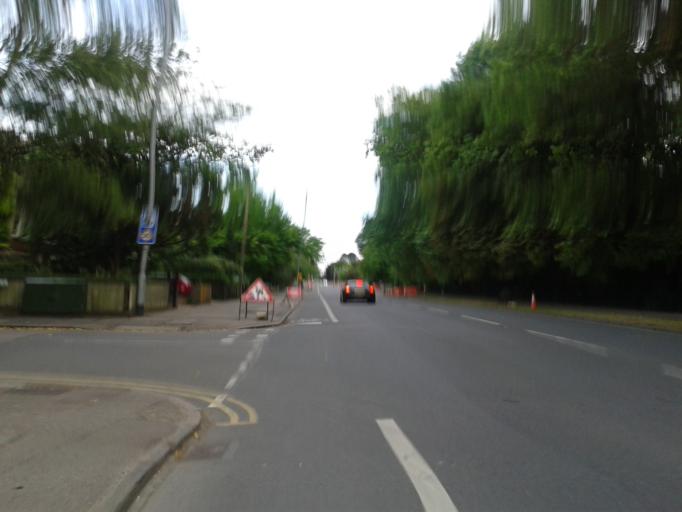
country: GB
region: England
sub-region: Cambridgeshire
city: Cambridge
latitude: 52.1866
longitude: 0.1378
